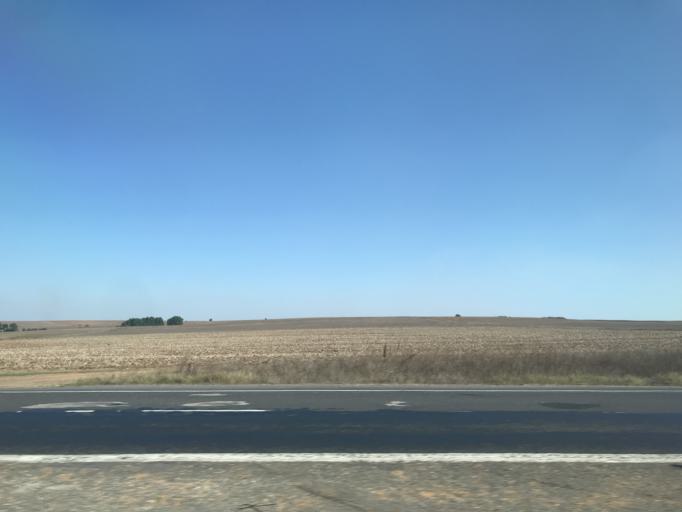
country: TR
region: Tekirdag
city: Muratli
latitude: 41.1139
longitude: 27.4915
